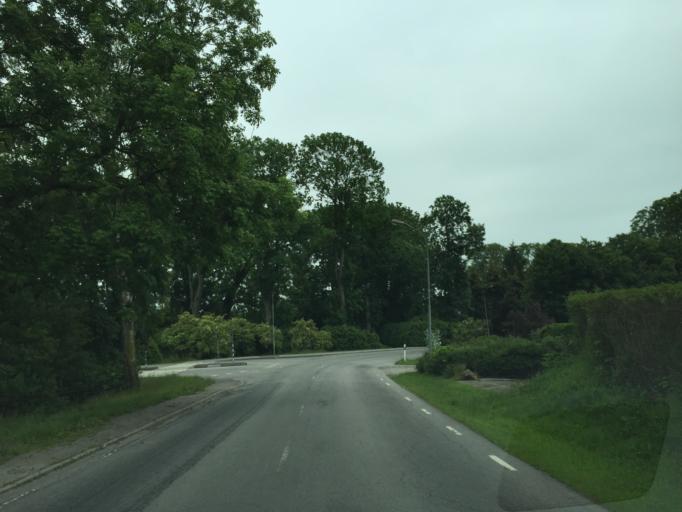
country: SE
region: Skane
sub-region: Ystads Kommun
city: Kopingebro
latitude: 55.4442
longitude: 14.1216
